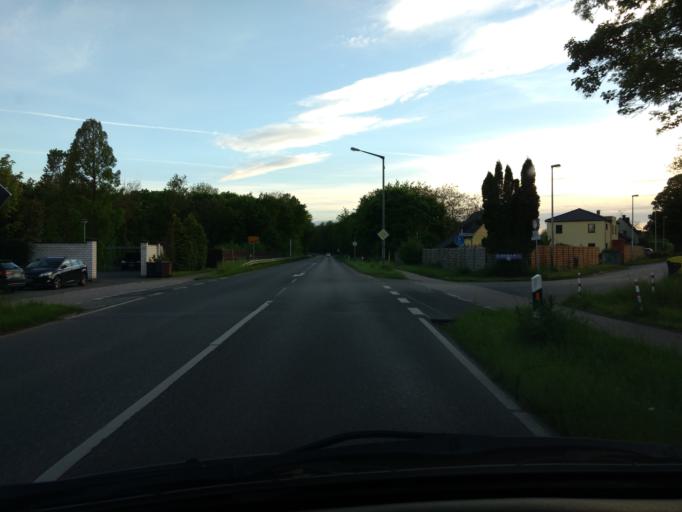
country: DE
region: North Rhine-Westphalia
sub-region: Regierungsbezirk Koln
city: Frechen
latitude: 50.9342
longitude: 6.7565
